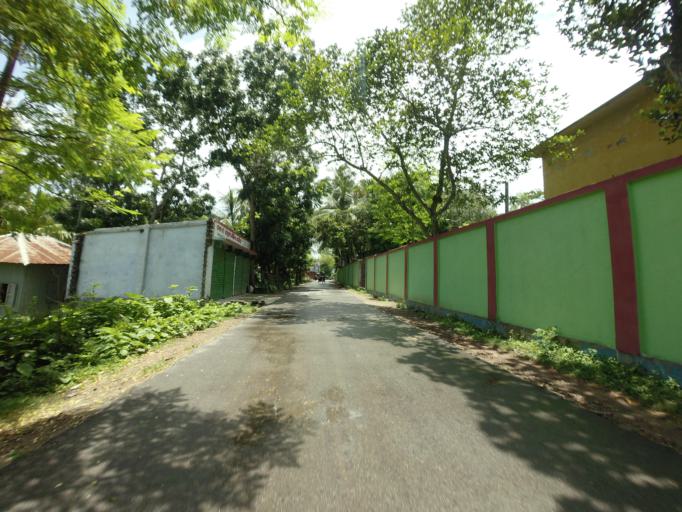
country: BD
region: Khulna
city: Kalia
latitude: 23.0406
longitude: 89.6349
